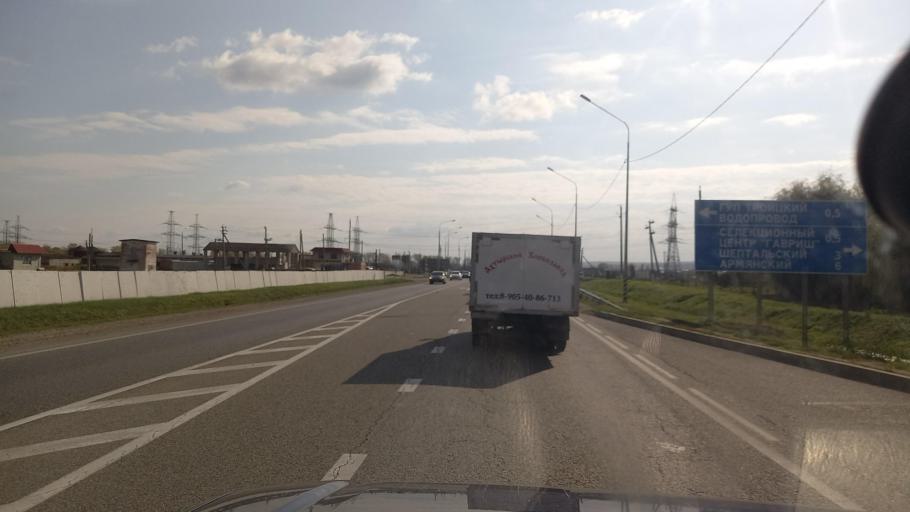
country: RU
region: Krasnodarskiy
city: Novoukrainskiy
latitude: 44.9065
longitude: 38.0269
